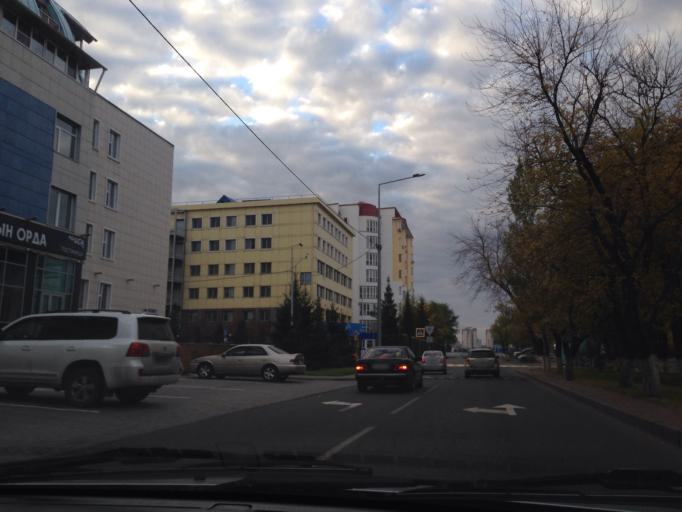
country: KZ
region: Astana Qalasy
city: Astana
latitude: 51.1621
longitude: 71.4239
